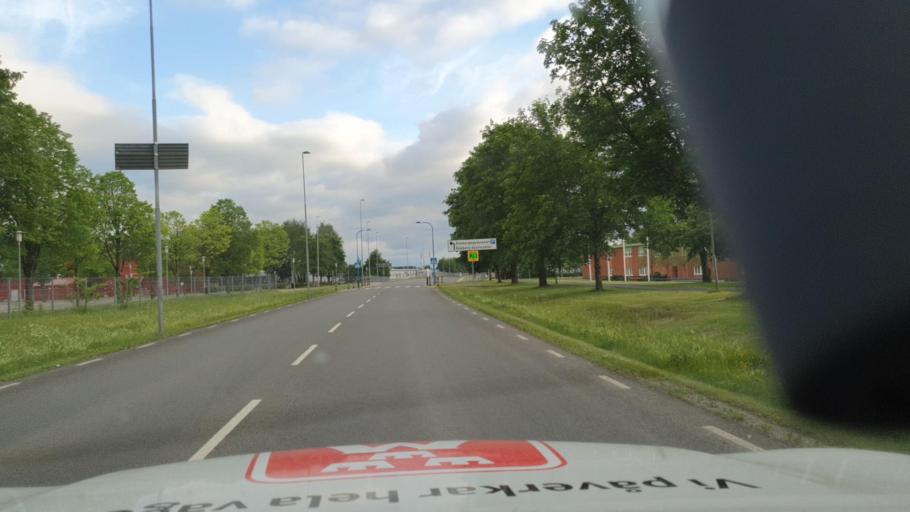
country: SE
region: Vaestra Goetaland
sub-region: Falkopings Kommun
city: Falkoeping
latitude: 58.1669
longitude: 13.5688
